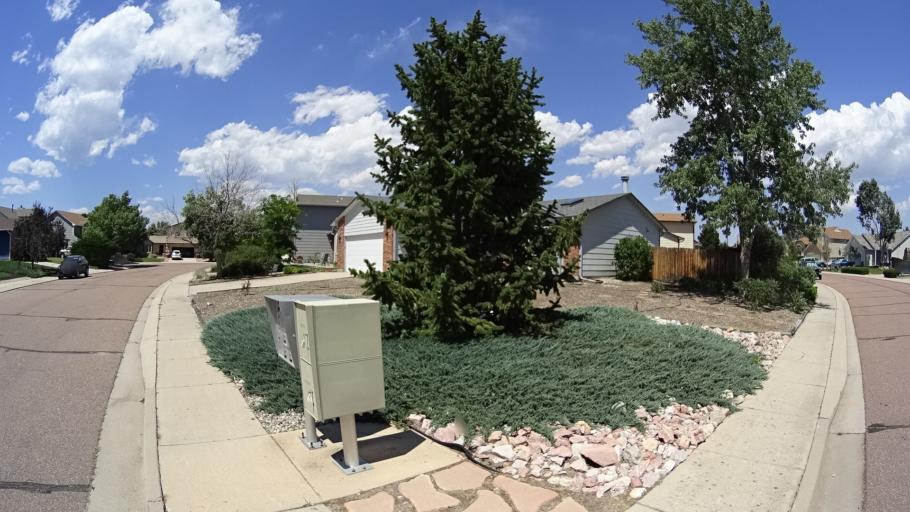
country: US
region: Colorado
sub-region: El Paso County
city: Black Forest
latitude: 38.9490
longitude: -104.7451
